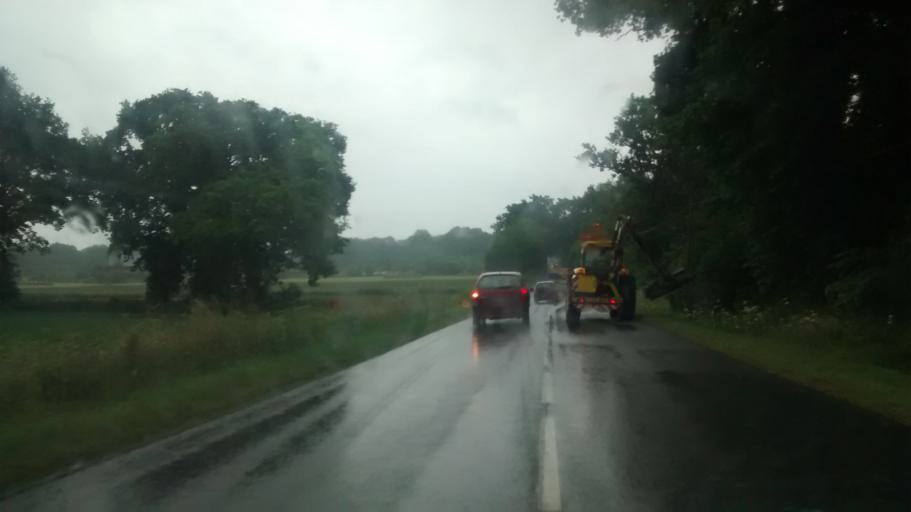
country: FR
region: Brittany
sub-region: Departement du Morbihan
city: La Gacilly
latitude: 47.7760
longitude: -2.1566
